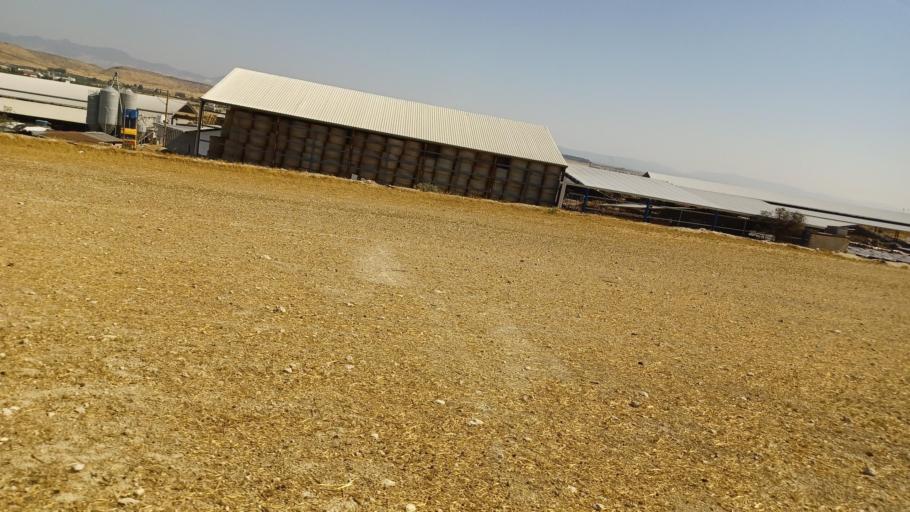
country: CY
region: Larnaka
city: Athienou
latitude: 35.0442
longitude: 33.5309
